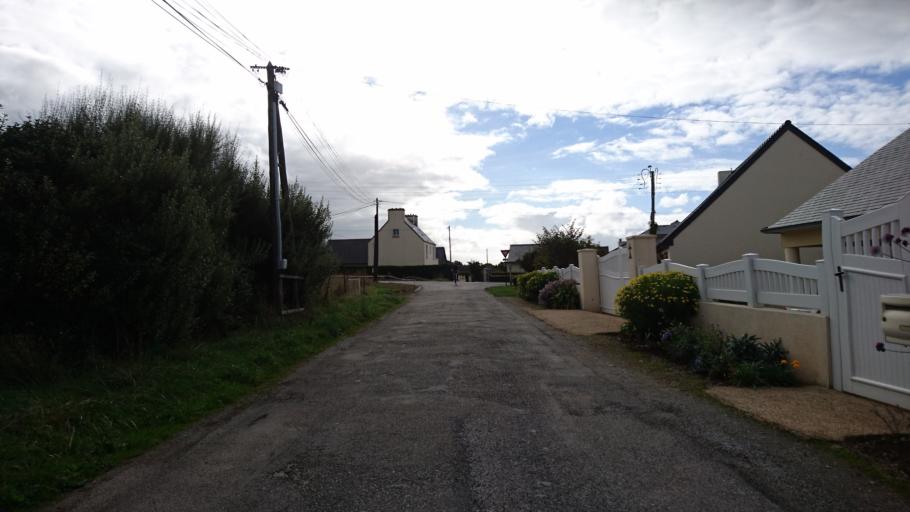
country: FR
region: Brittany
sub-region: Departement du Finistere
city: Lampaul-Plouarzel
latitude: 48.4449
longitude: -4.7658
